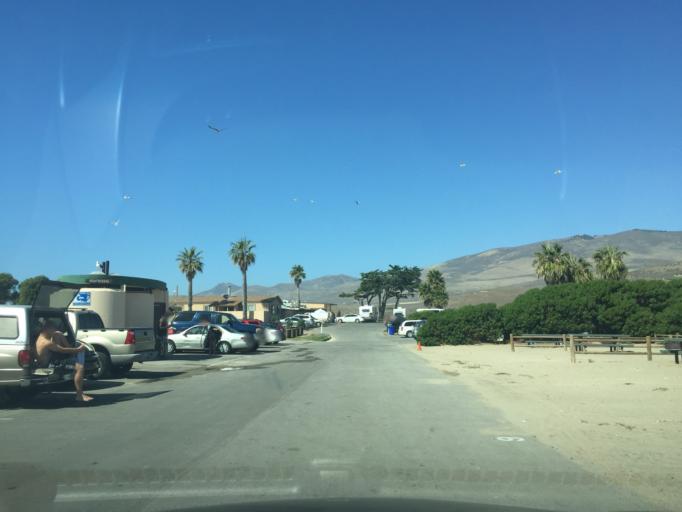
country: US
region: California
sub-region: Santa Barbara County
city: Lompoc
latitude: 34.5106
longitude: -120.5015
